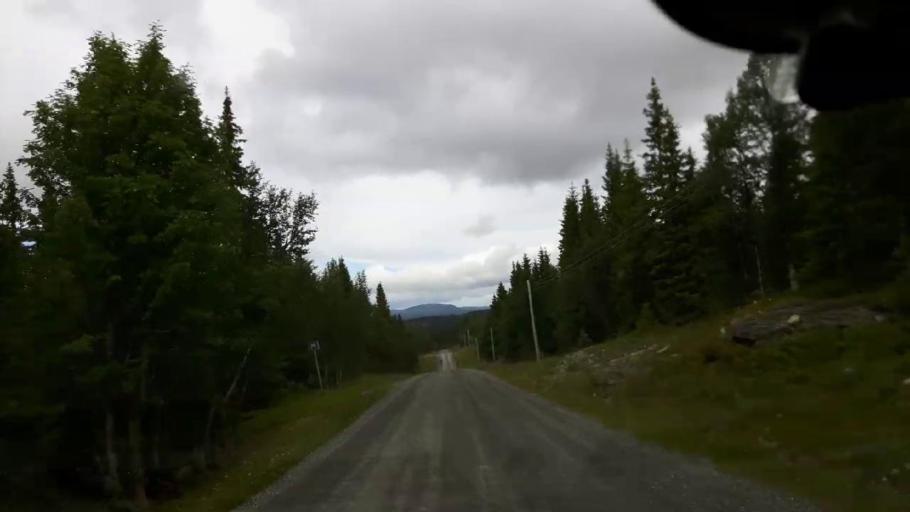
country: SE
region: Jaemtland
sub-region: Krokoms Kommun
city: Valla
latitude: 63.7731
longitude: 13.8296
